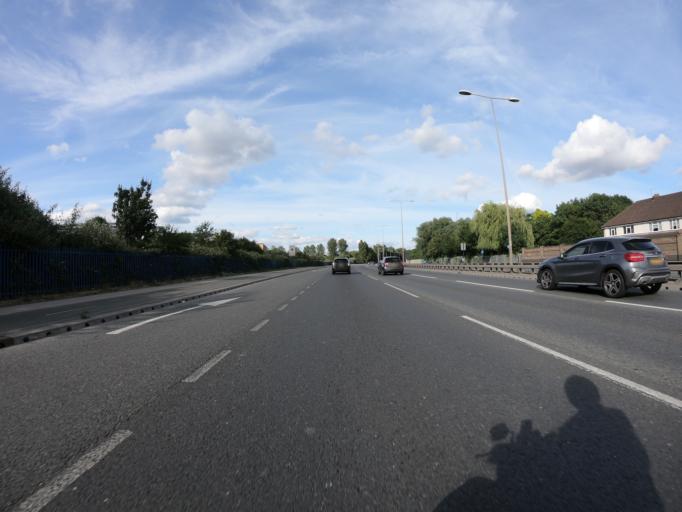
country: GB
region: England
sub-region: Greater London
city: East Ham
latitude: 51.5187
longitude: 0.0380
